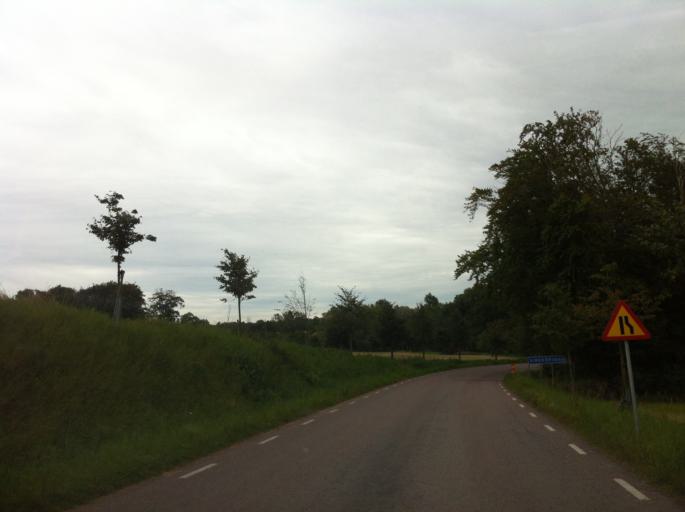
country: SE
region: Skane
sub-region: Landskrona
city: Asmundtorp
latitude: 55.9301
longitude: 12.9902
